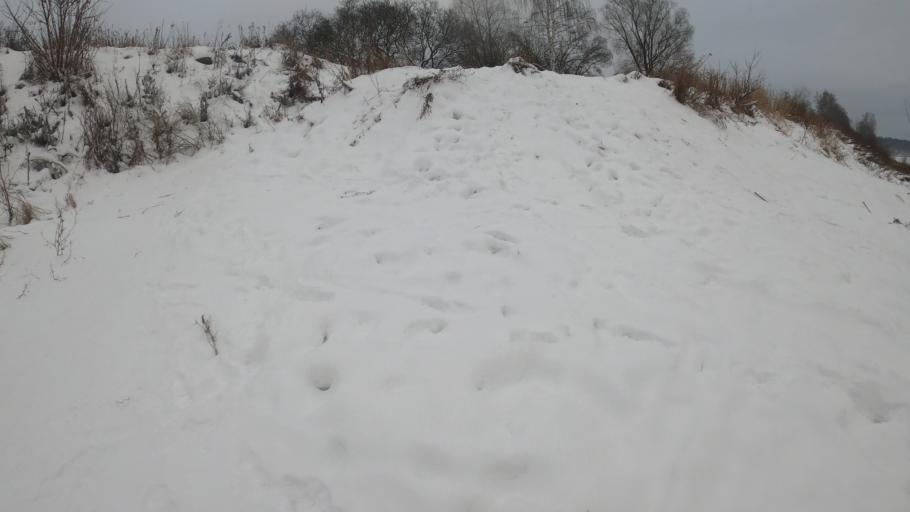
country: RU
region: Moskovskaya
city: Dolgoprudnyy
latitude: 55.9425
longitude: 37.4811
